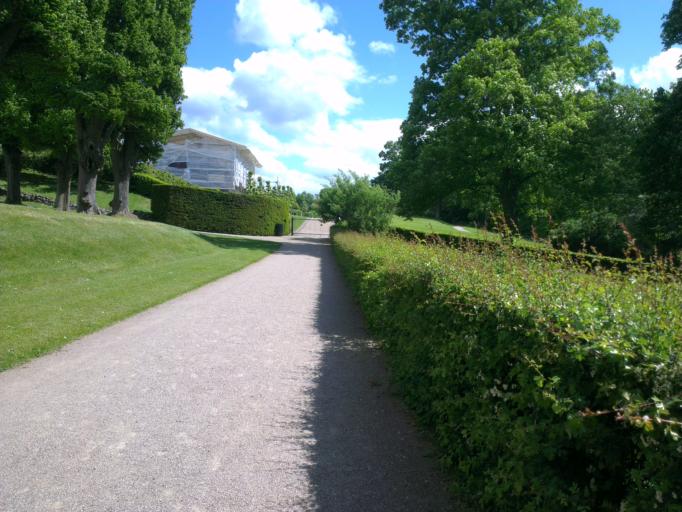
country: DK
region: Capital Region
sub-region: Hillerod Kommune
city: Hillerod
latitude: 55.9365
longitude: 12.3058
